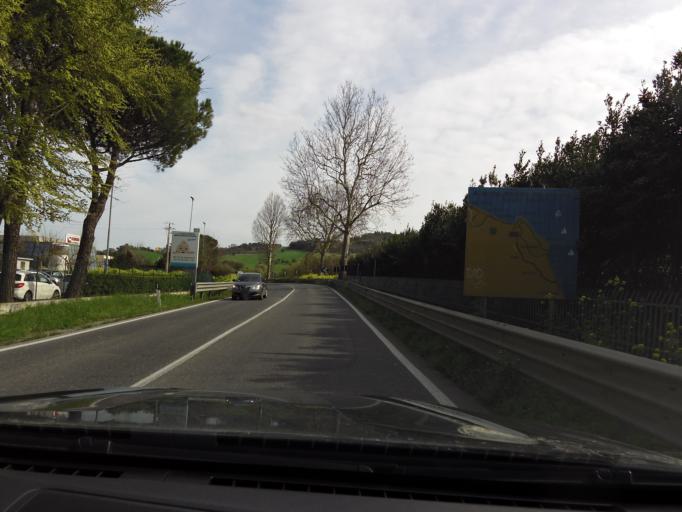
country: IT
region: The Marches
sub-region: Provincia di Ancona
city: Castelfidardo
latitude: 43.4931
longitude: 13.5546
